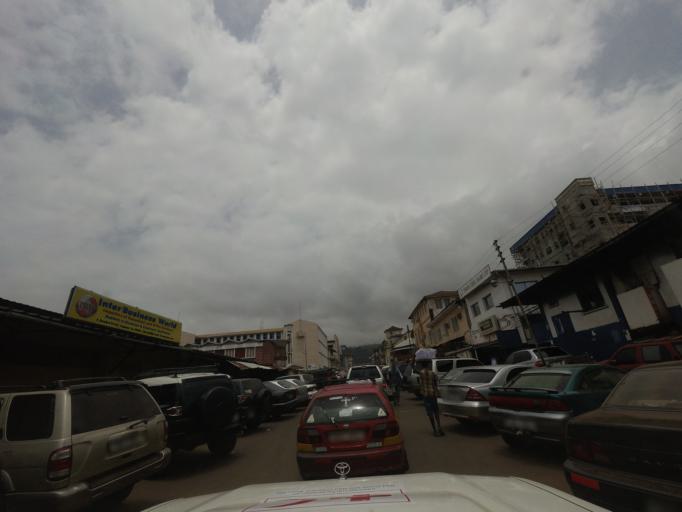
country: SL
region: Western Area
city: Freetown
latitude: 8.4913
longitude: -13.2340
